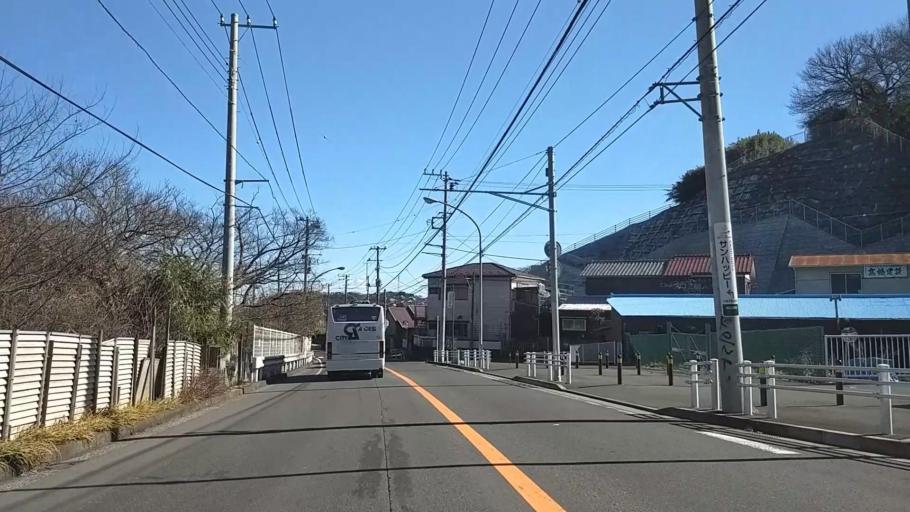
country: JP
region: Kanagawa
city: Zushi
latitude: 35.3294
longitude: 139.5963
